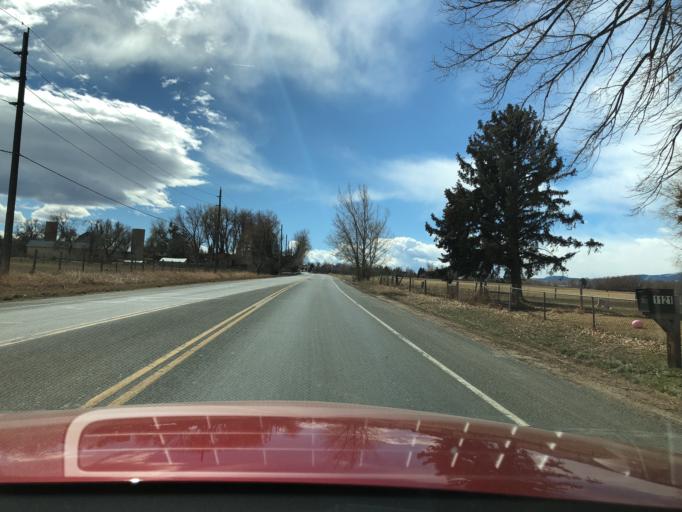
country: US
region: Colorado
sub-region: Boulder County
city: Louisville
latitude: 40.0073
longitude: -105.1783
